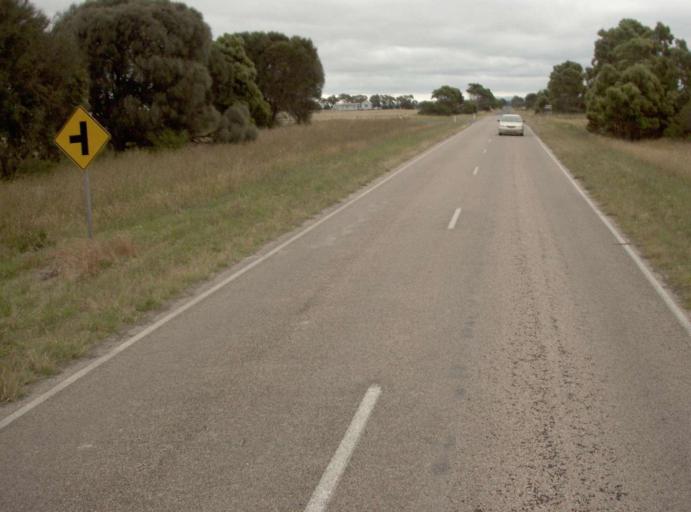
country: AU
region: Victoria
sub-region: Wellington
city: Sale
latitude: -38.5389
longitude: 146.9184
